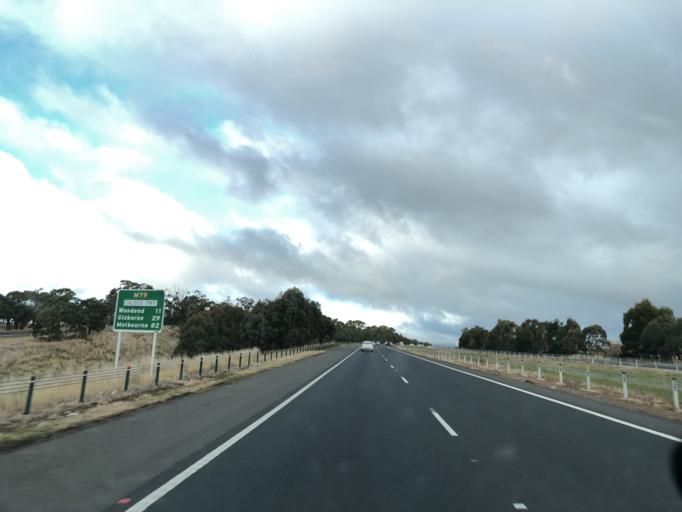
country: AU
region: Victoria
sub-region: Mount Alexander
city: Castlemaine
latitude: -37.2724
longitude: 144.4807
